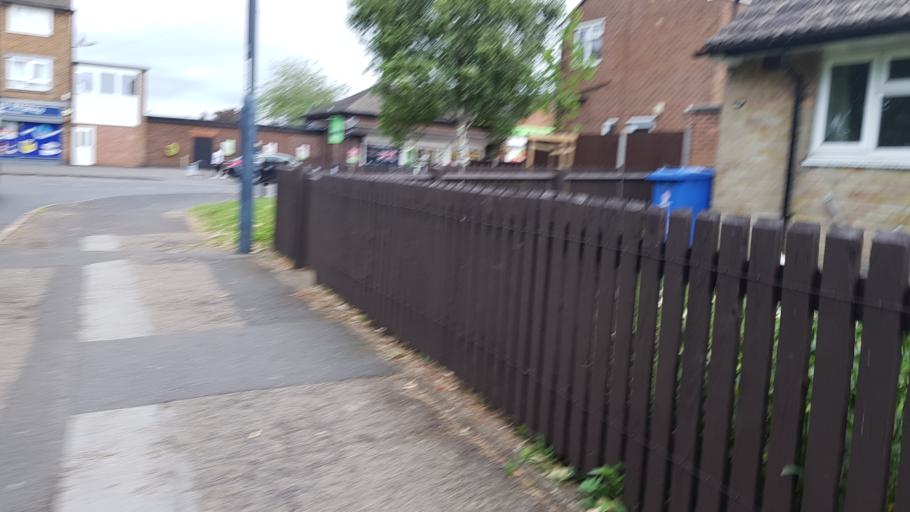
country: GB
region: England
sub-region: Derby
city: Derby
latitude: 52.8879
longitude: -1.4360
